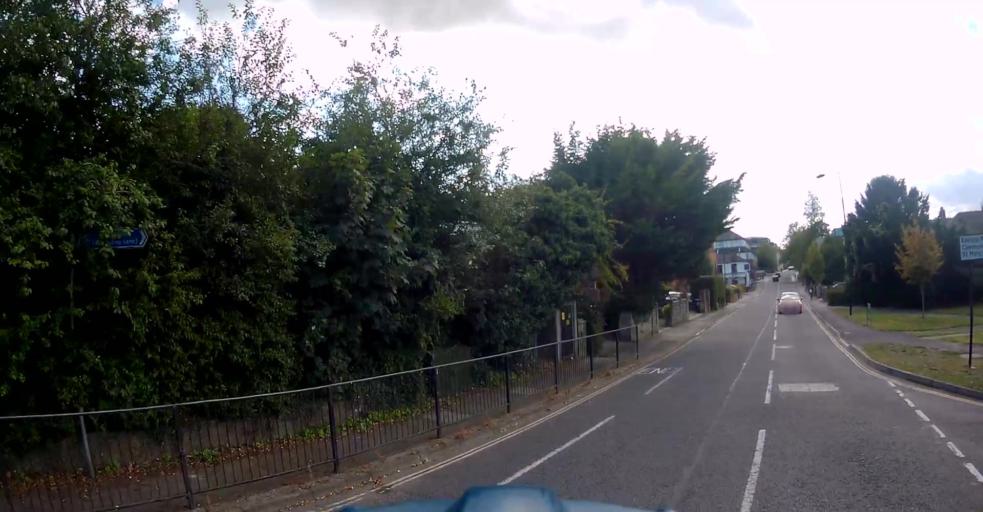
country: GB
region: England
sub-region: Hampshire
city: Basingstoke
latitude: 51.2628
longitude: -1.0806
